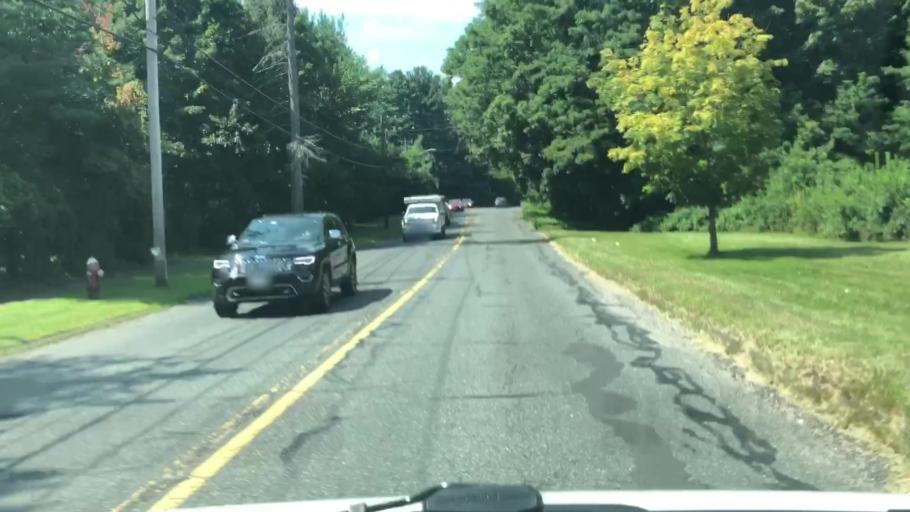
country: US
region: Massachusetts
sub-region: Hampshire County
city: Northampton
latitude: 42.3391
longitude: -72.6567
